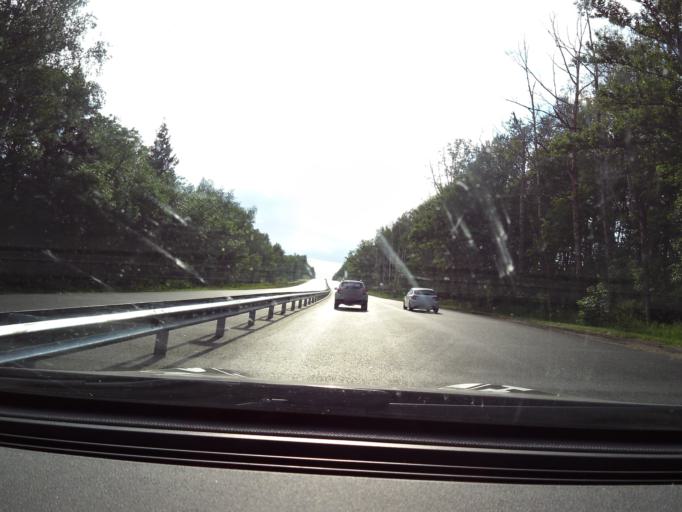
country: RU
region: Vladimir
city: Novovyazniki
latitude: 56.2029
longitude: 42.3485
